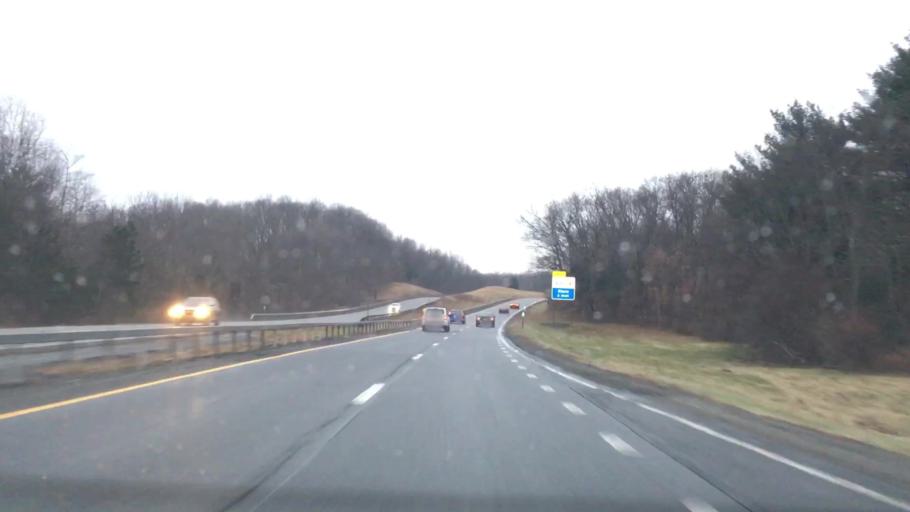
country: US
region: New York
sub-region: Dutchess County
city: Hillside Lake
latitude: 41.6267
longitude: -73.7767
